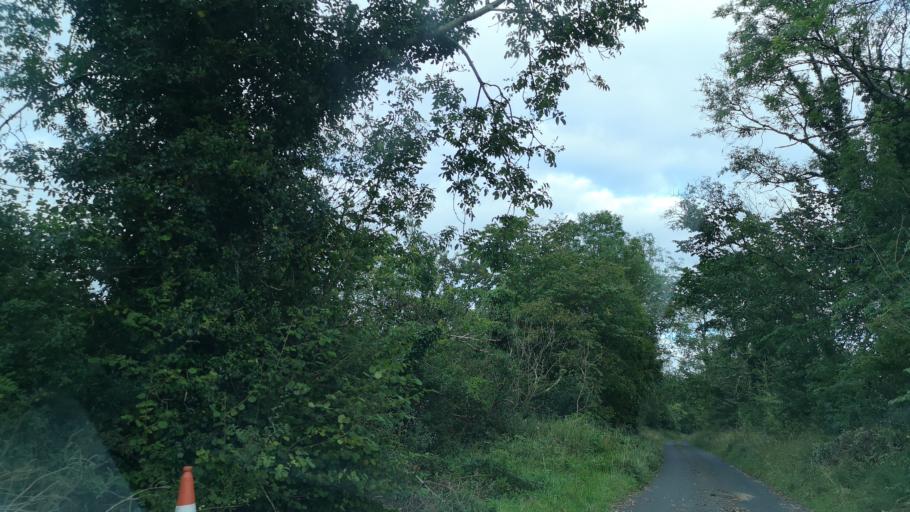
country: IE
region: Connaught
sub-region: County Galway
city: Loughrea
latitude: 53.1484
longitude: -8.5026
